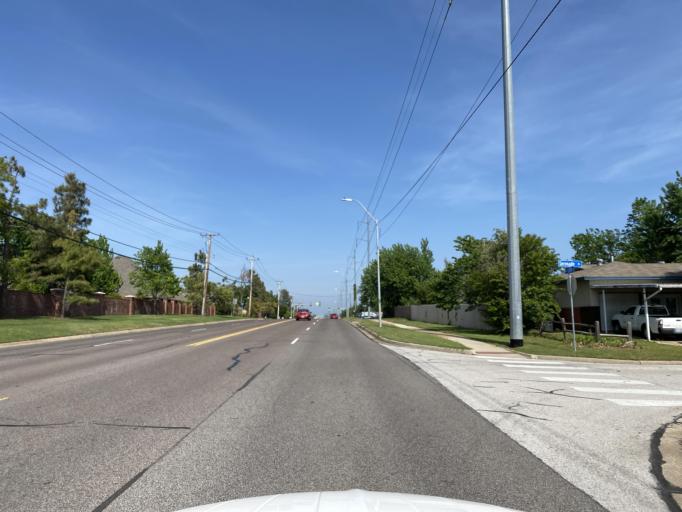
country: US
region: Oklahoma
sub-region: Oklahoma County
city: Midwest City
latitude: 35.4496
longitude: -97.3639
